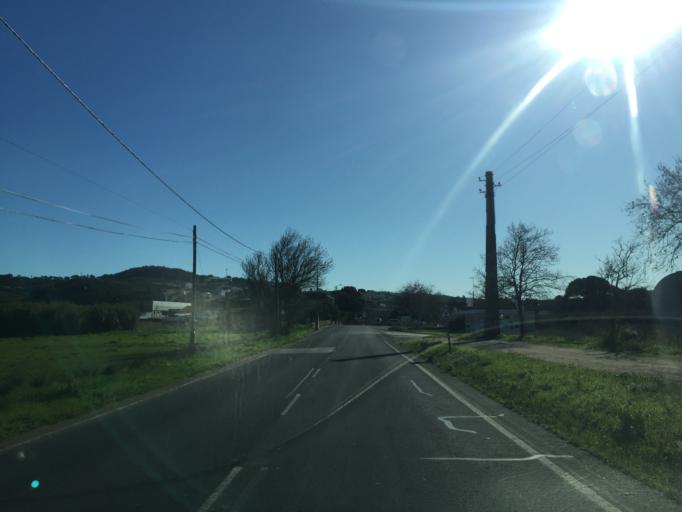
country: PT
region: Lisbon
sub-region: Sintra
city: Pero Pinheiro
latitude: 38.8308
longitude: -9.3048
